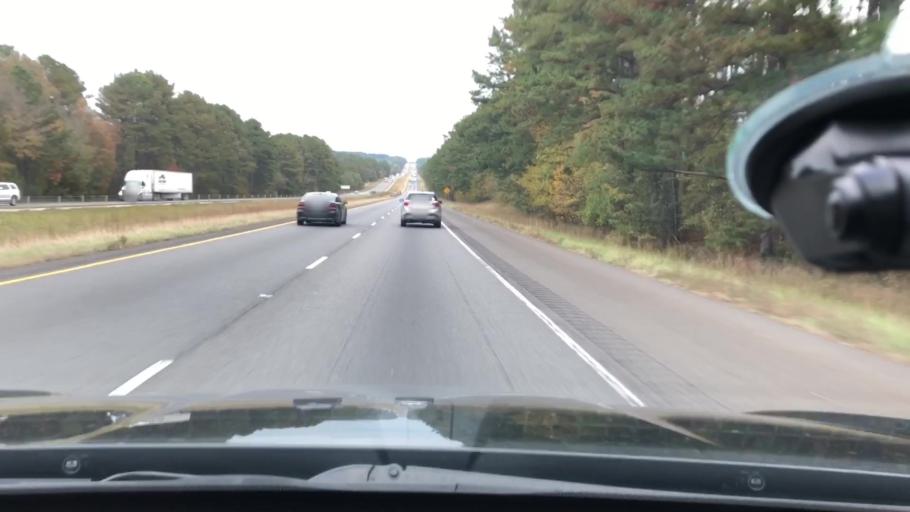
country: US
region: Arkansas
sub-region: Clark County
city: Arkadelphia
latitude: 34.2488
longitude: -92.9934
